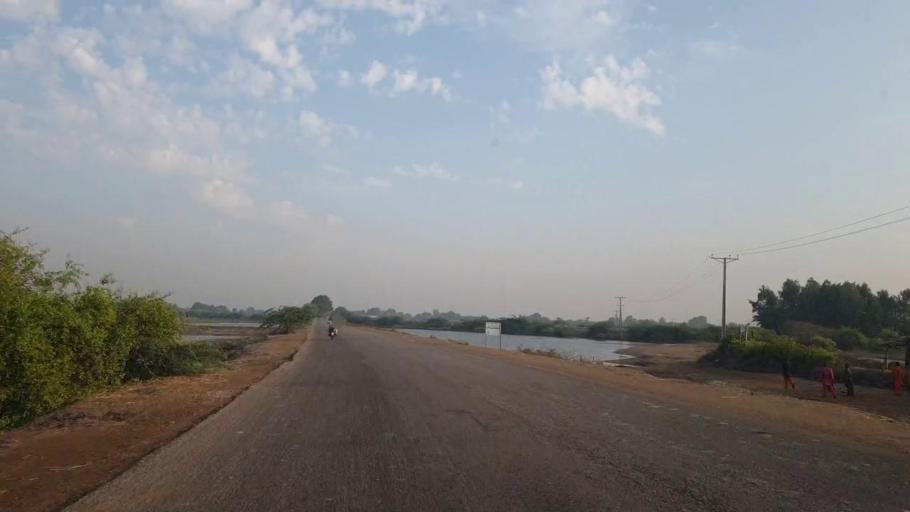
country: PK
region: Sindh
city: Tando Bago
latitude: 24.7123
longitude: 68.9387
